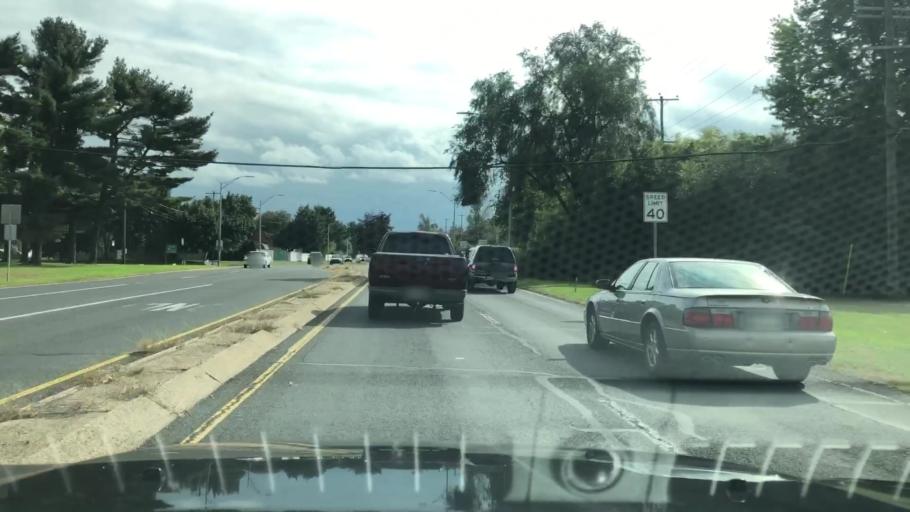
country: US
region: Pennsylvania
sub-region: Bucks County
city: Levittown
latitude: 40.1552
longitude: -74.8286
